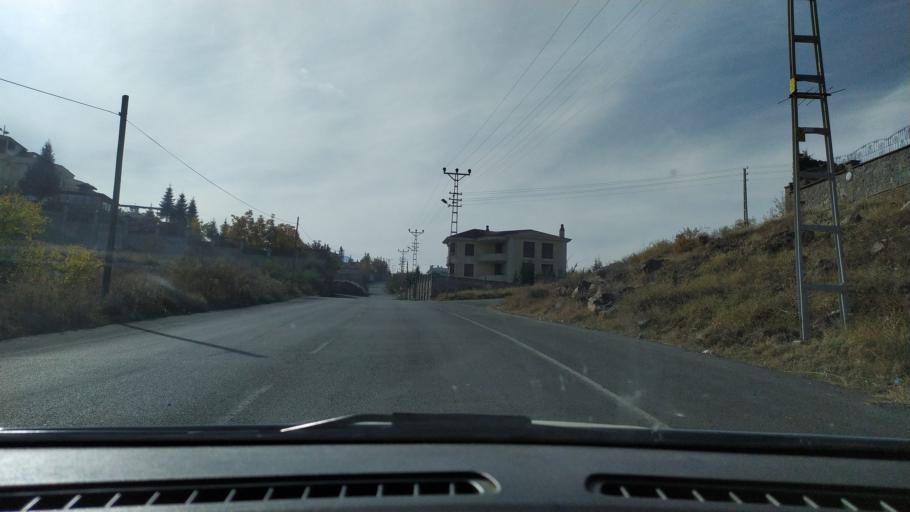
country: TR
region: Kayseri
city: Kayseri
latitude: 38.6802
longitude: 35.4914
